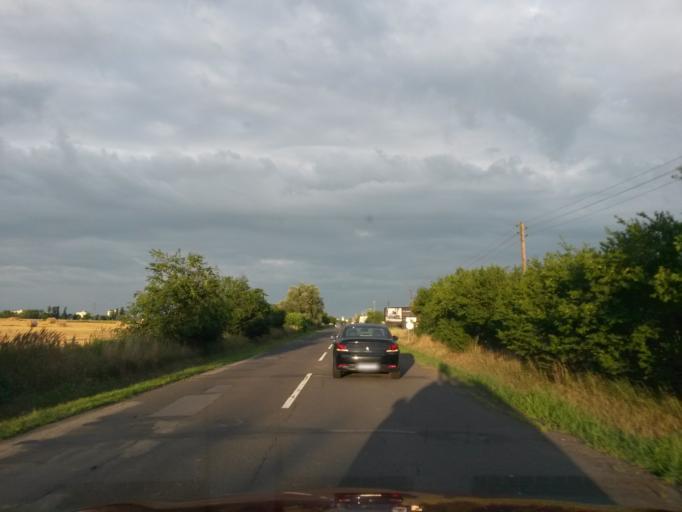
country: SK
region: Banskobystricky
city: Lucenec
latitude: 48.3368
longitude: 19.6236
